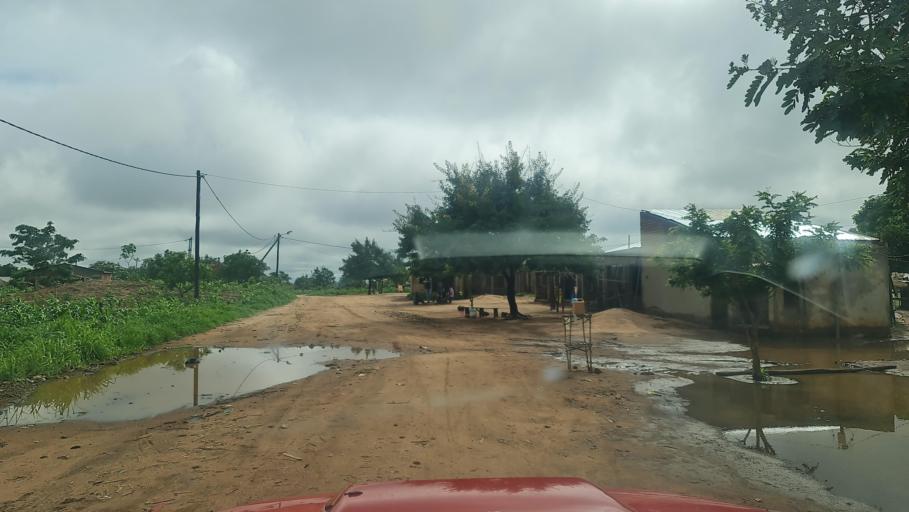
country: MW
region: Southern Region
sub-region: Nsanje District
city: Nsanje
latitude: -17.2210
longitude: 35.6714
